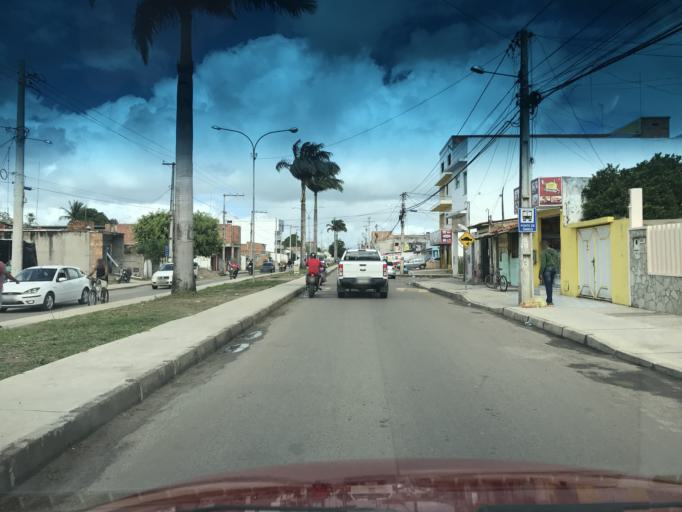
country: BR
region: Bahia
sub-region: Santo Antonio De Jesus
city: Santo Antonio de Jesus
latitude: -12.9699
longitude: -39.2716
